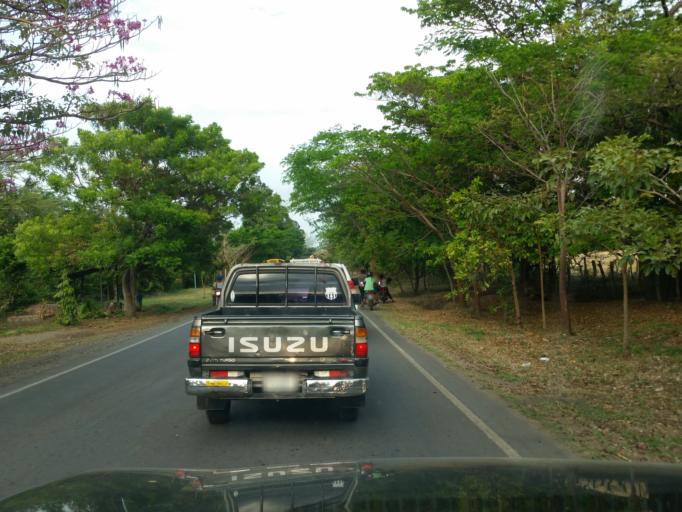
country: NI
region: Rivas
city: Rivas
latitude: 11.4416
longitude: -85.8452
